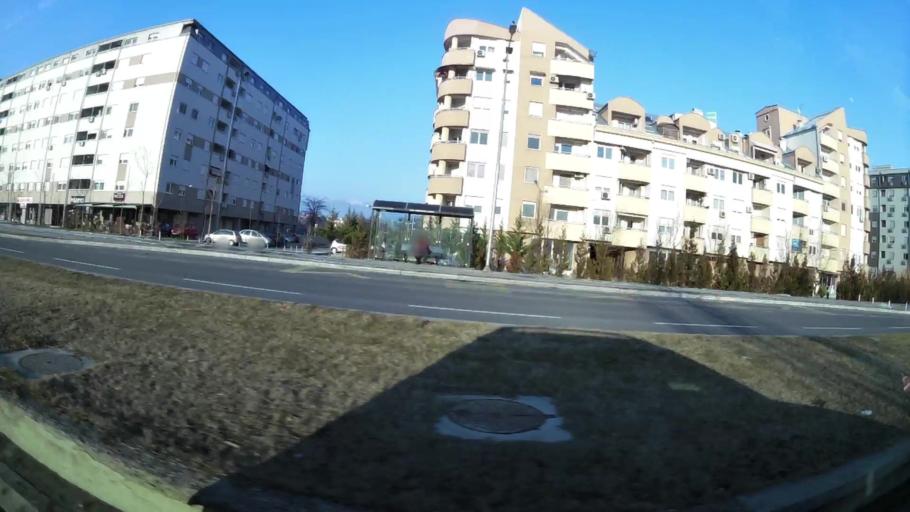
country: MK
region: Kisela Voda
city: Usje
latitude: 41.9805
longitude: 21.4575
